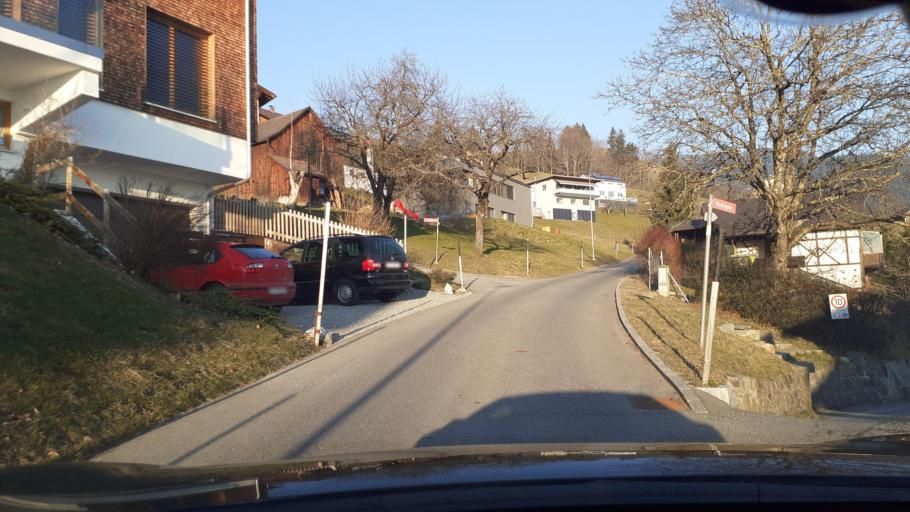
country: AT
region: Vorarlberg
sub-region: Politischer Bezirk Feldkirch
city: Fraxern
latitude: 47.3180
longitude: 9.6760
